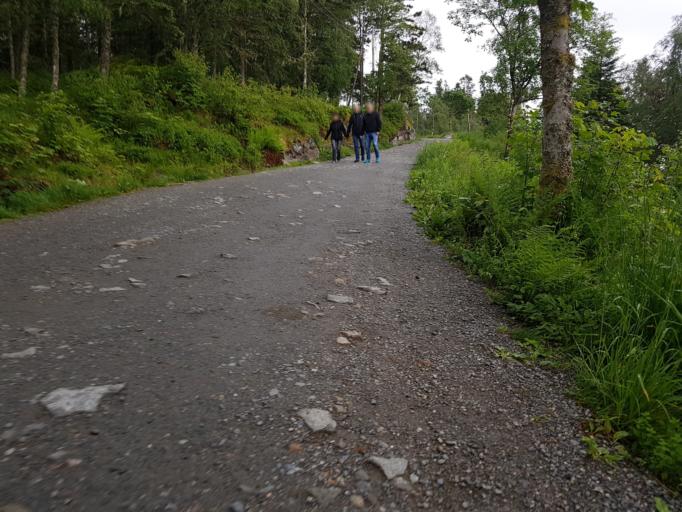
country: NO
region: Hordaland
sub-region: Bergen
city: Bergen
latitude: 60.3968
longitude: 5.3399
